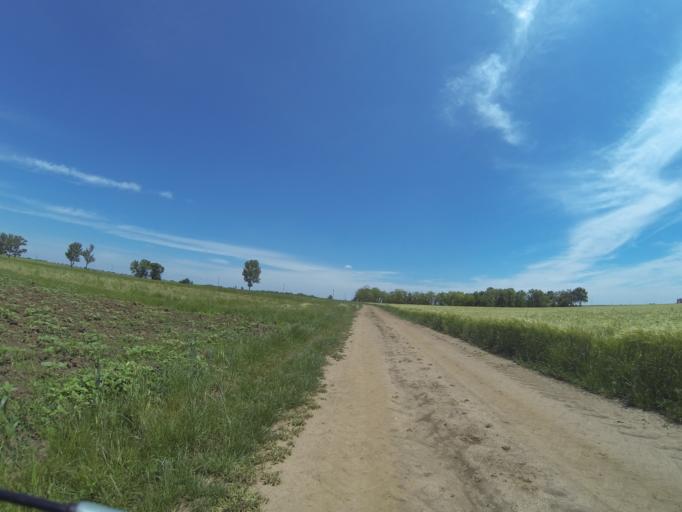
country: RO
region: Dolj
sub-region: Comuna Diosti
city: Radomir
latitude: 44.1461
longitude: 24.1619
